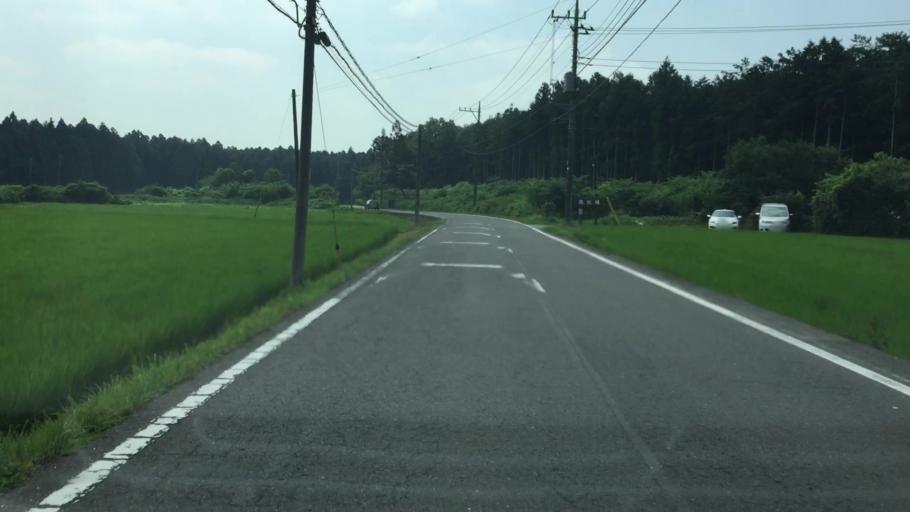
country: JP
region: Tochigi
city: Kuroiso
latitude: 36.9568
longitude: 139.9566
